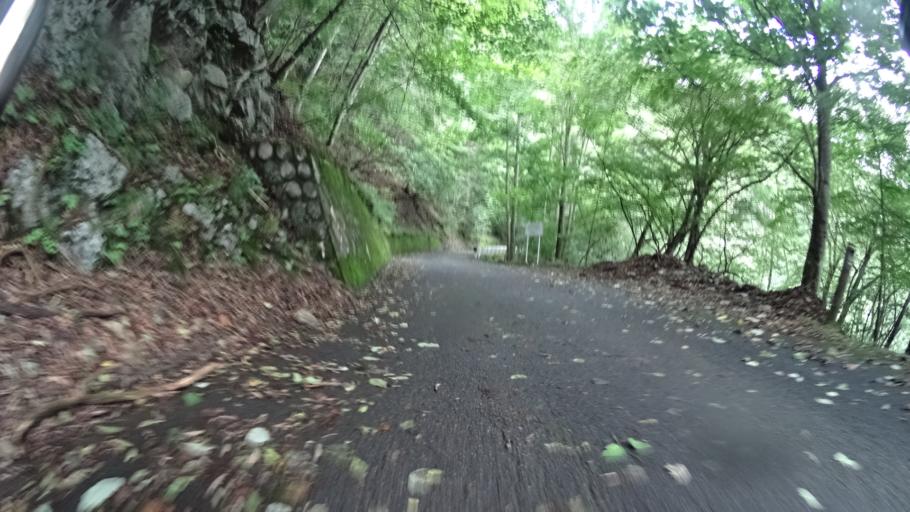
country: JP
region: Saitama
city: Chichibu
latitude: 35.8814
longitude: 139.1123
